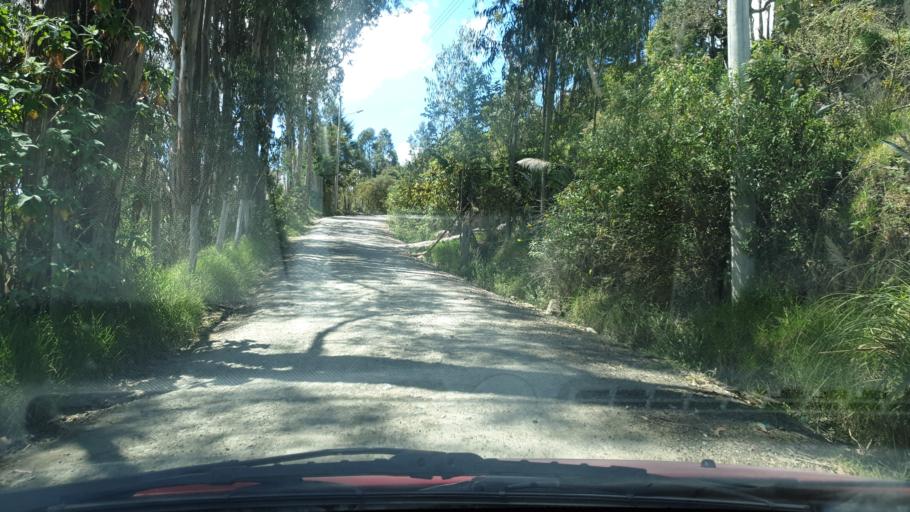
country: EC
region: Azuay
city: Llacao
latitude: -2.8767
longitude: -78.9046
